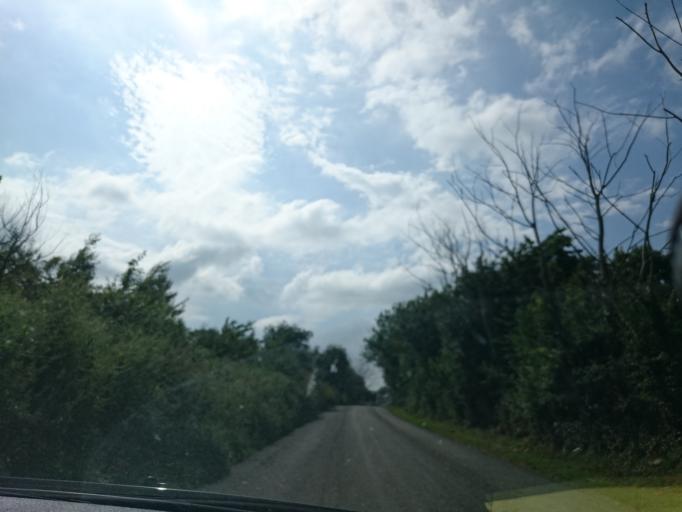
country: IE
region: Leinster
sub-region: Kilkenny
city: Thomastown
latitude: 52.5208
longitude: -7.1958
